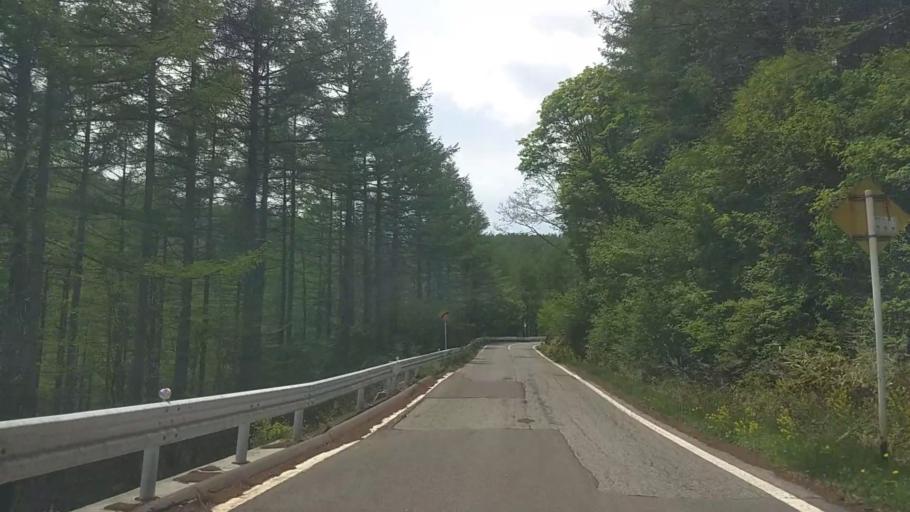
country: JP
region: Nagano
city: Saku
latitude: 36.0945
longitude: 138.3885
